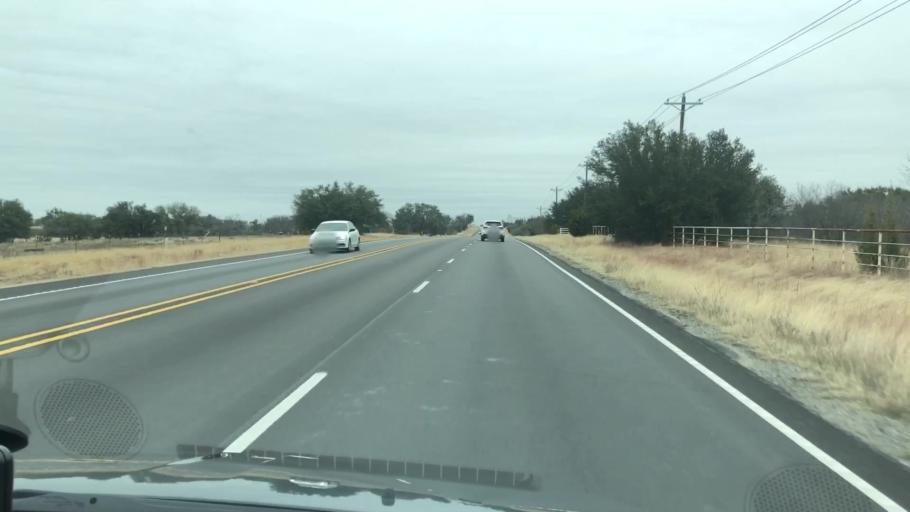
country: US
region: Texas
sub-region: Erath County
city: Stephenville
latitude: 32.3206
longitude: -98.1815
